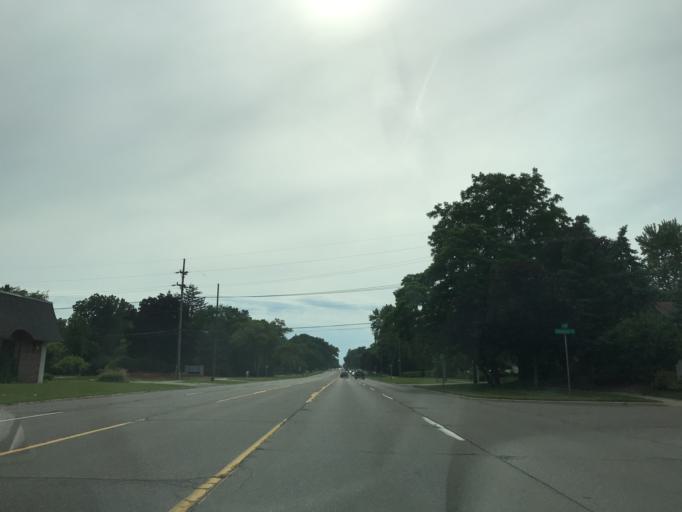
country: US
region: Michigan
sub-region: Wayne County
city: Livonia
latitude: 42.4125
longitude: -83.3438
